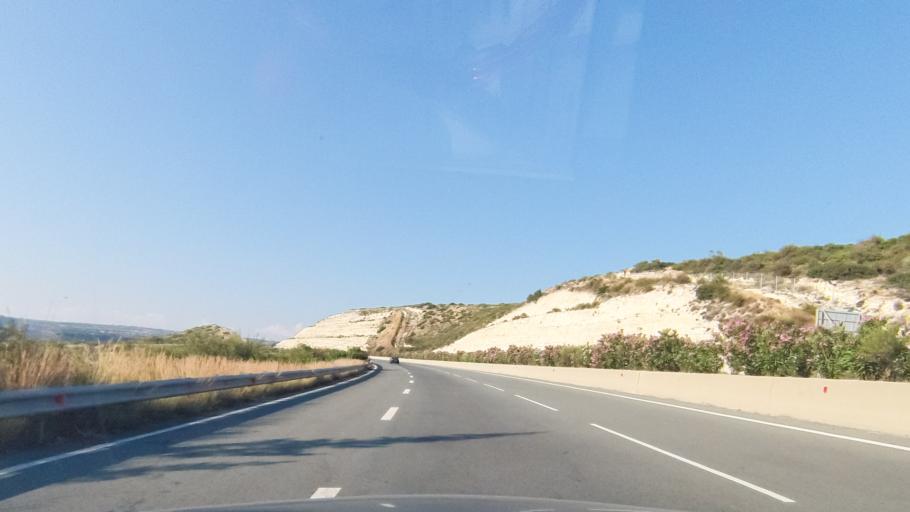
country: CY
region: Limassol
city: Sotira
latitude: 34.6800
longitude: 32.8035
